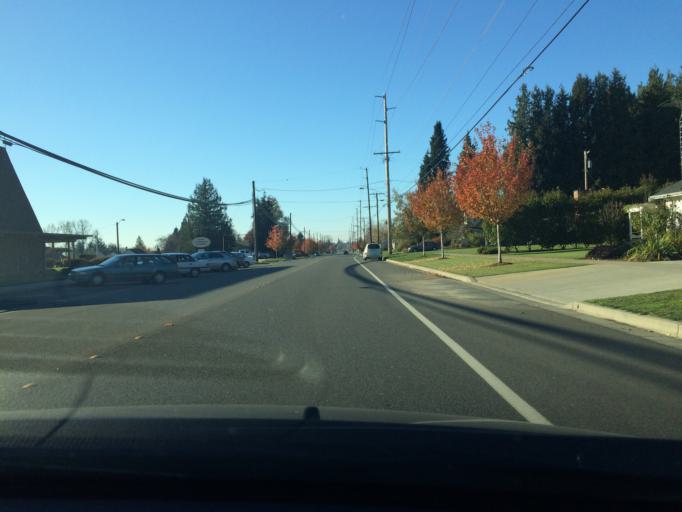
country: US
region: Washington
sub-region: Whatcom County
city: Lynden
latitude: 48.9485
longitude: -122.4380
